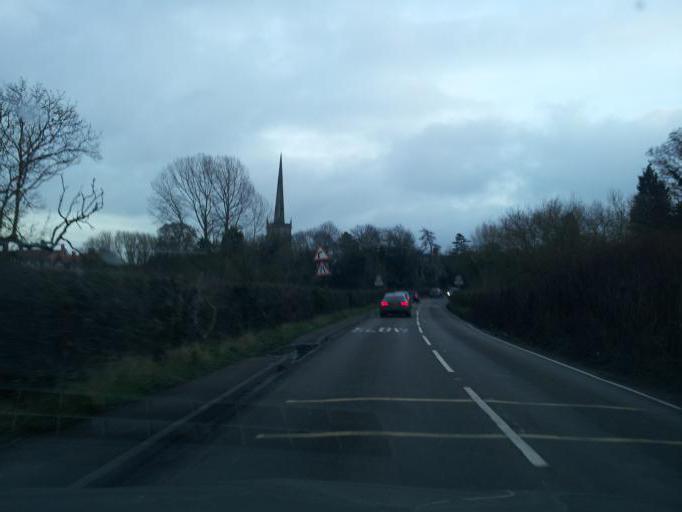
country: GB
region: England
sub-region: Derbyshire
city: Repton
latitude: 52.8425
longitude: -1.5553
